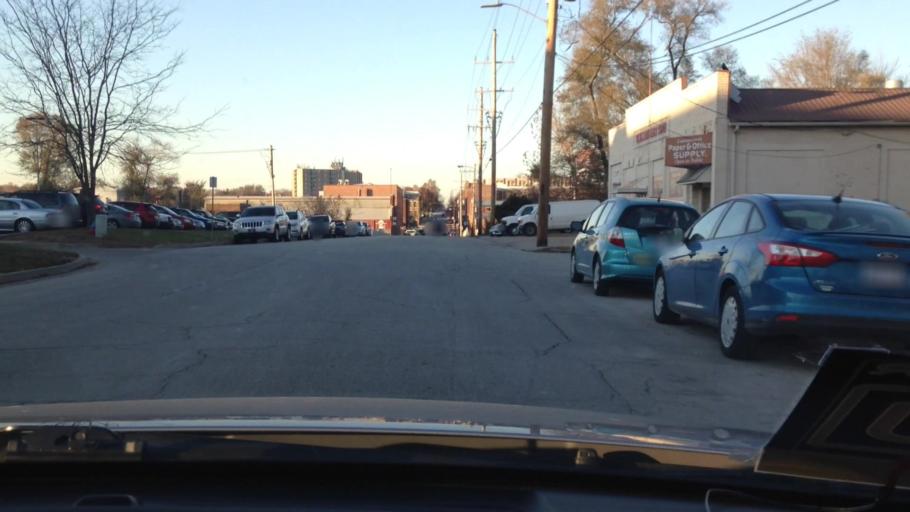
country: US
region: Kansas
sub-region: Leavenworth County
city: Leavenworth
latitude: 39.3141
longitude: -94.9097
